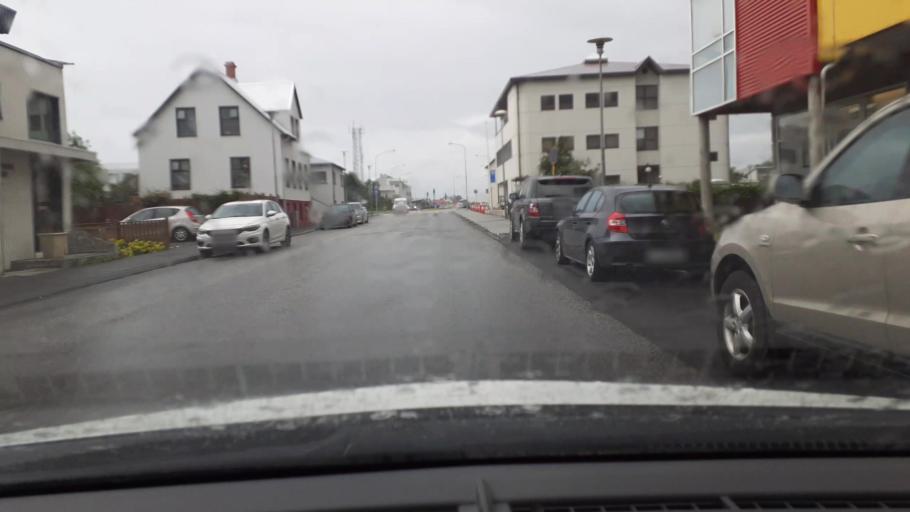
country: IS
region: West
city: Akranes
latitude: 64.3183
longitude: -22.0813
